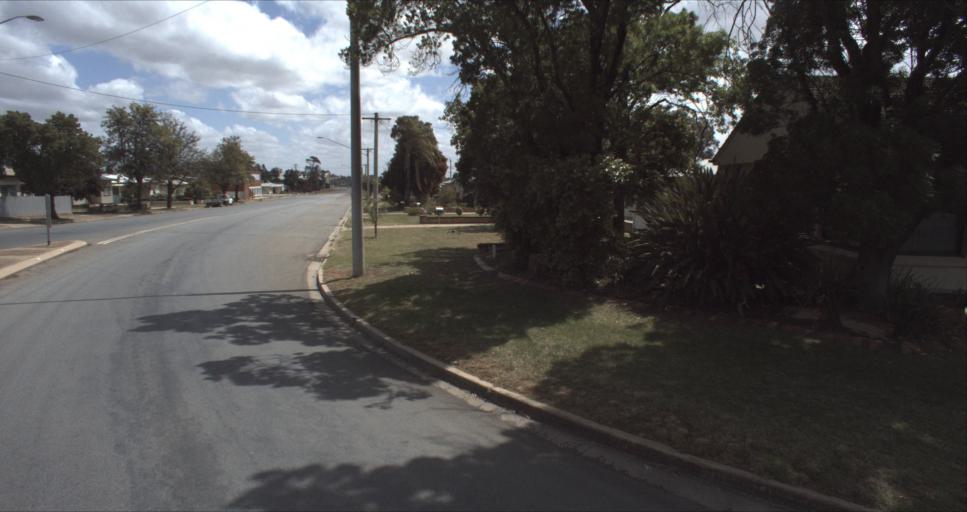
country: AU
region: New South Wales
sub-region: Leeton
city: Leeton
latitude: -34.5568
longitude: 146.4000
